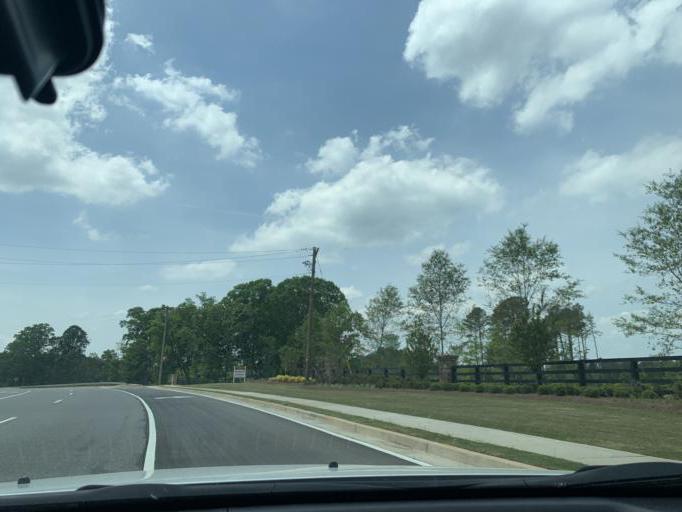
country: US
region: Georgia
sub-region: Forsyth County
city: Cumming
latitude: 34.1554
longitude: -84.1661
